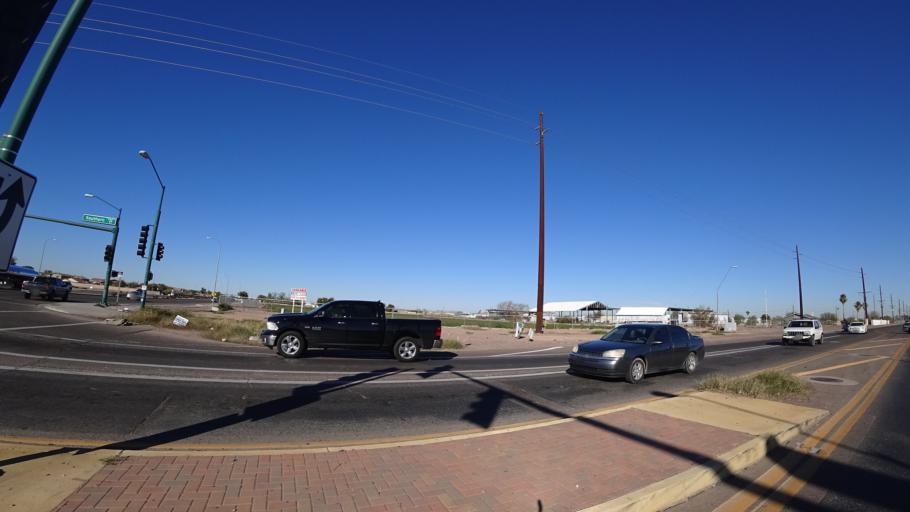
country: US
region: Arizona
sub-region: Maricopa County
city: Laveen
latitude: 33.3919
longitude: -112.1680
